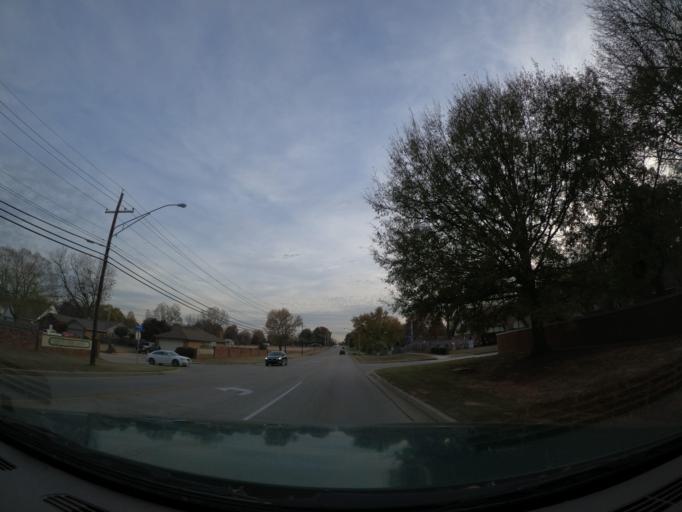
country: US
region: Oklahoma
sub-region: Tulsa County
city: Broken Arrow
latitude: 35.9818
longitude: -95.7974
